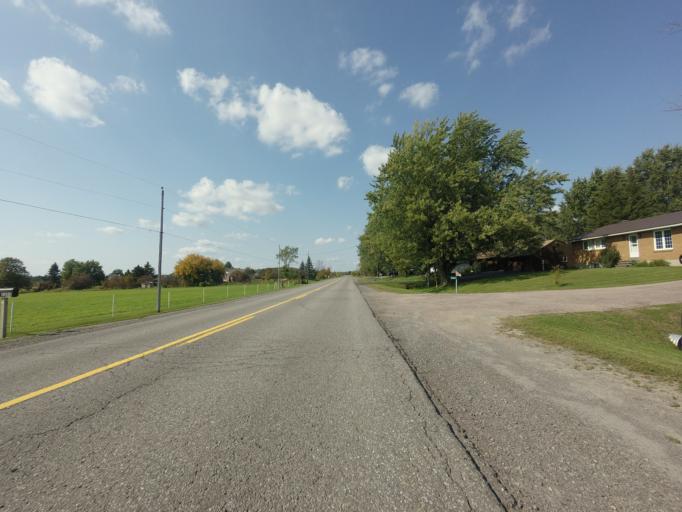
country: CA
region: Ontario
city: Ottawa
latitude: 45.2392
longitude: -75.6719
